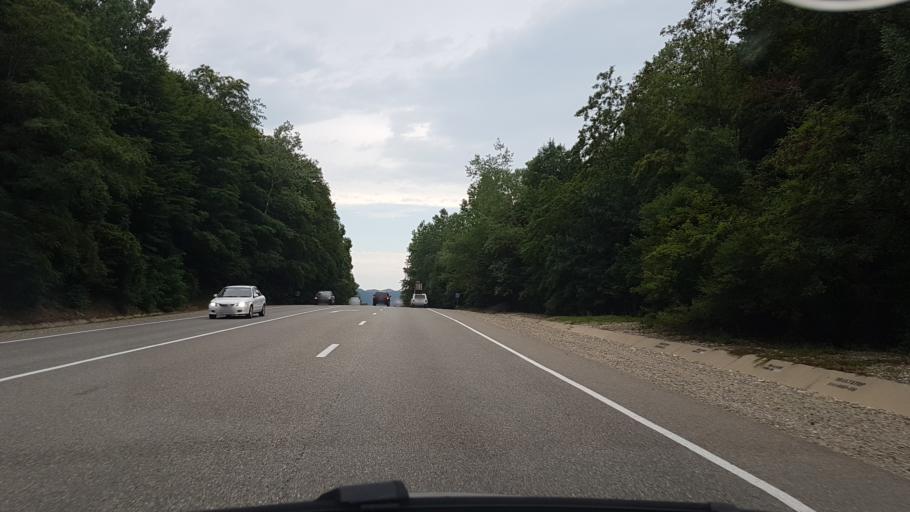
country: RU
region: Krasnodarskiy
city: Lermontovo
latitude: 44.4557
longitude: 38.8053
